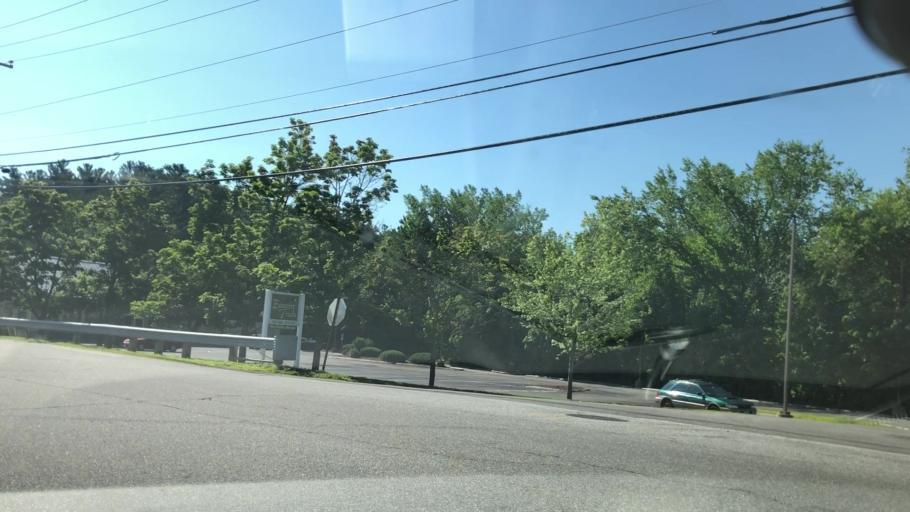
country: US
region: New Hampshire
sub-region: Hillsborough County
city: Milford
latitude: 42.8235
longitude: -71.6260
